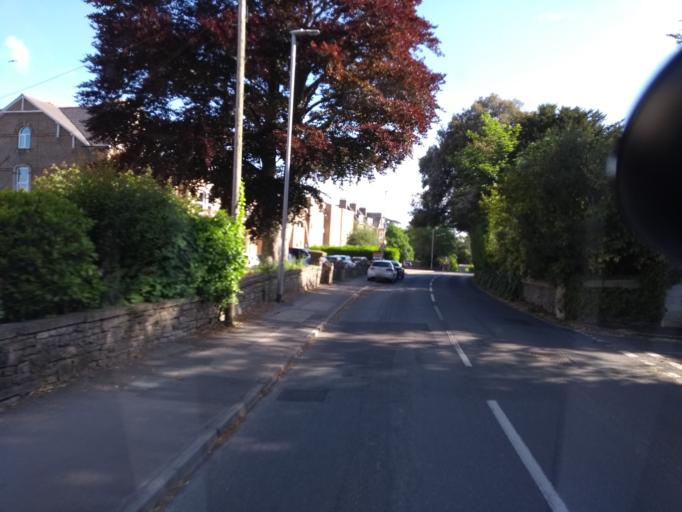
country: GB
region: England
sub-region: Somerset
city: Taunton
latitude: 51.0065
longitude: -3.1127
